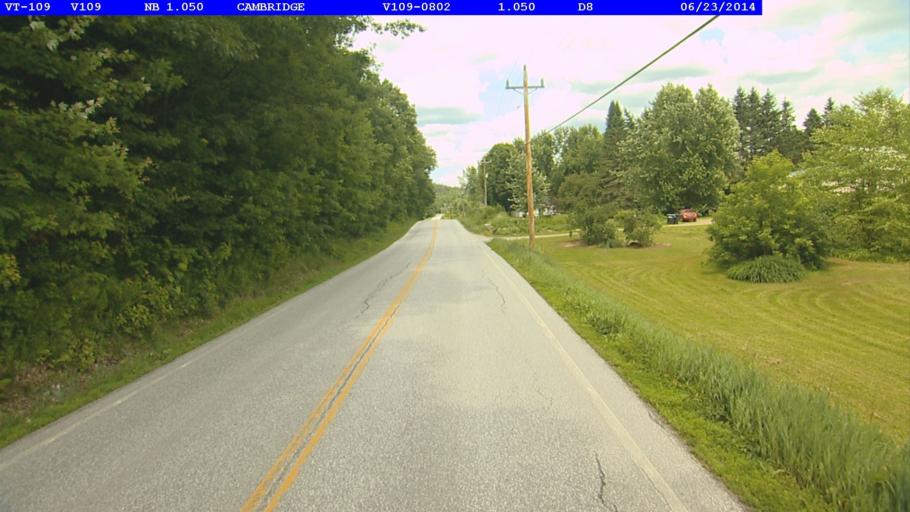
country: US
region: Vermont
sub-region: Lamoille County
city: Johnson
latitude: 44.6562
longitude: -72.8096
